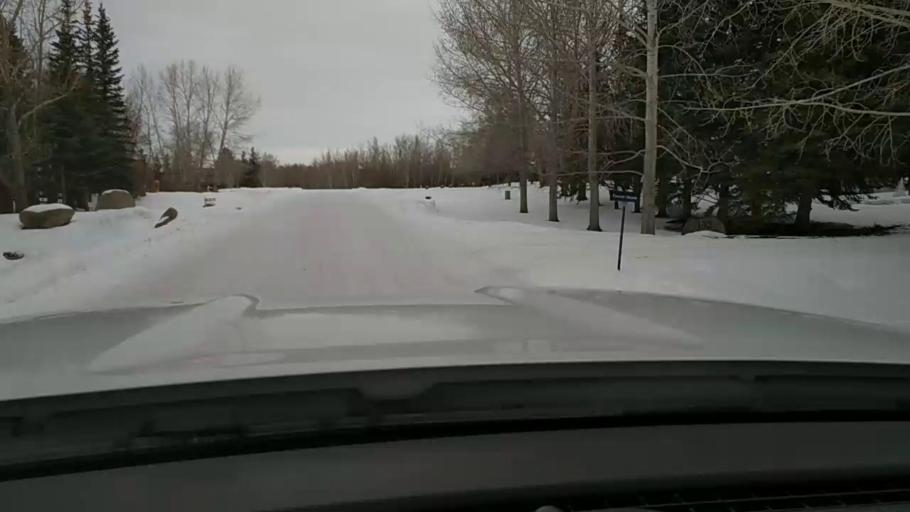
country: CA
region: Alberta
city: Calgary
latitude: 51.1178
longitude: -114.2668
